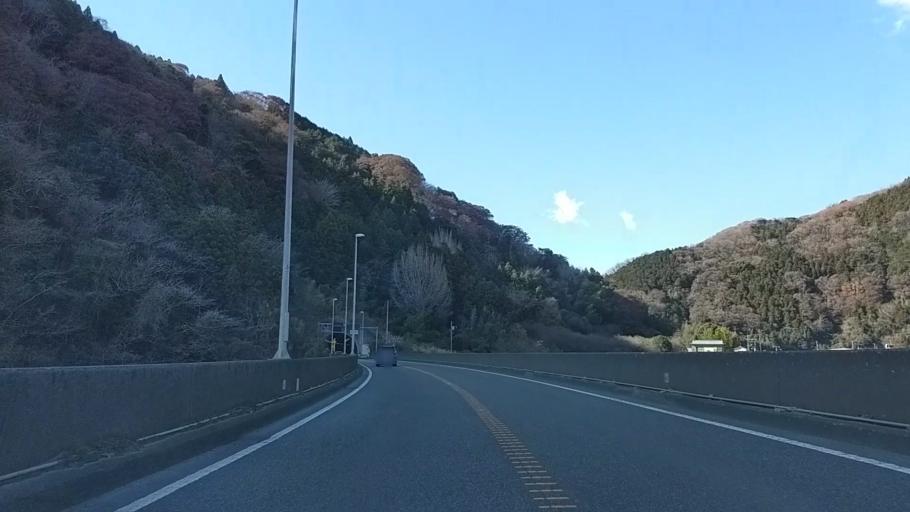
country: JP
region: Shizuoka
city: Gotemba
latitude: 35.3602
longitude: 139.0574
